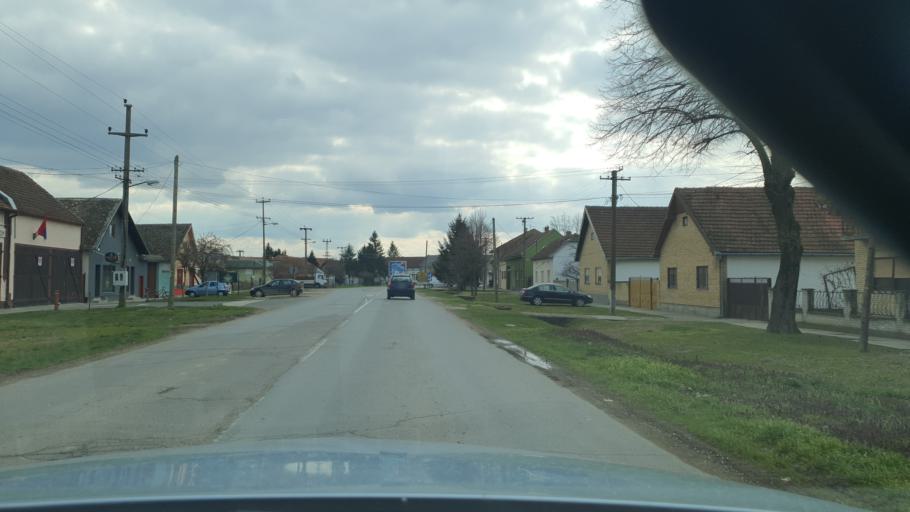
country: RS
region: Autonomna Pokrajina Vojvodina
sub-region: Juznobacki Okrug
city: Bac
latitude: 45.3932
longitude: 19.2372
